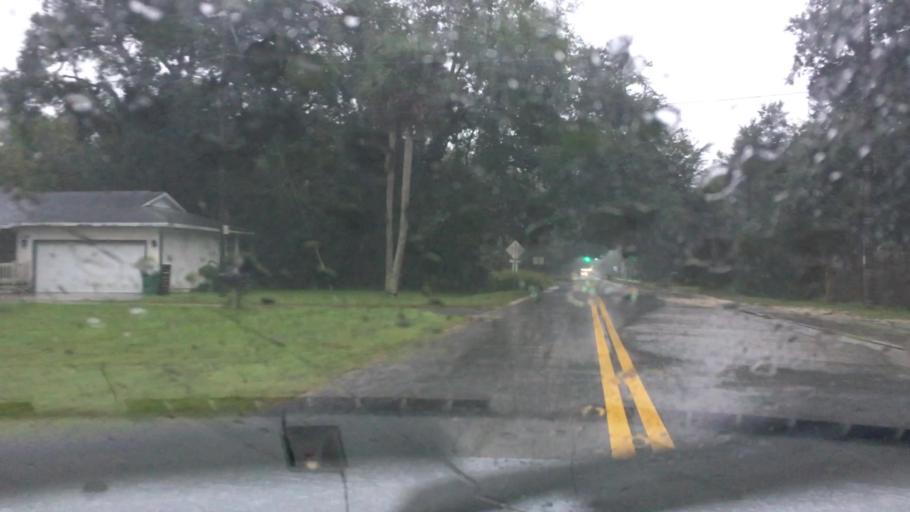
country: US
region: Florida
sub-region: Volusia County
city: Holly Hill
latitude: 29.2274
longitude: -81.0420
